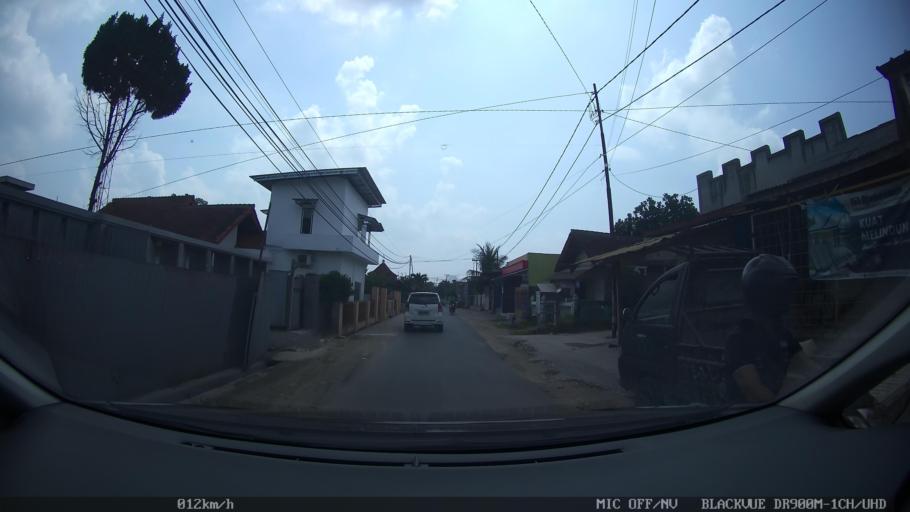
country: ID
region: Lampung
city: Pringsewu
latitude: -5.3577
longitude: 104.9725
